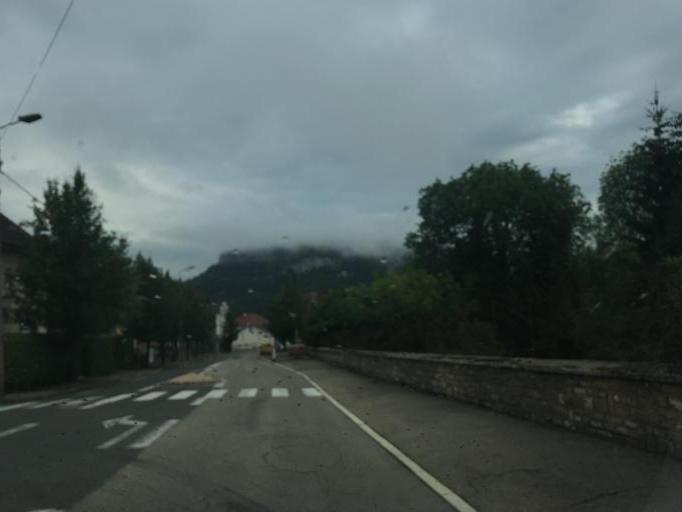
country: FR
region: Rhone-Alpes
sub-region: Departement de l'Ain
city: Dortan
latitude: 46.3143
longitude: 5.6591
